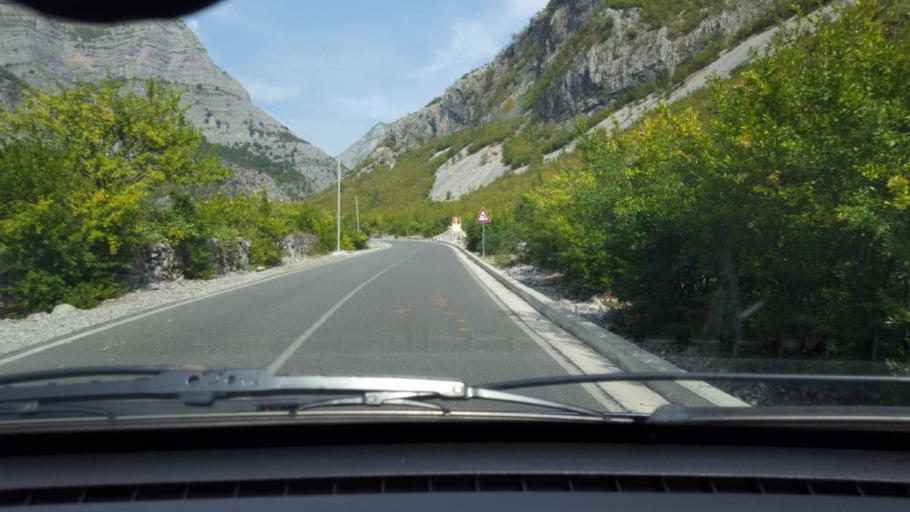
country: AL
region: Shkoder
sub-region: Rrethi i Malesia e Madhe
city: Kastrat
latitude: 42.4668
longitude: 19.5670
